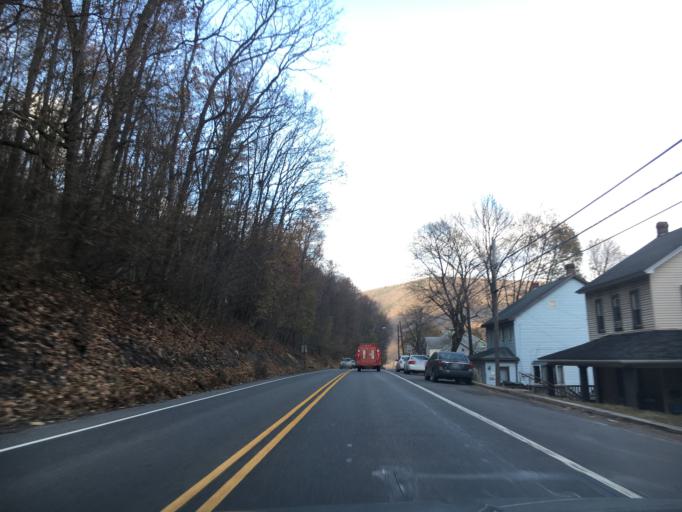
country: US
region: Pennsylvania
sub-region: Carbon County
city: Lehighton
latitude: 40.8465
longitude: -75.7115
